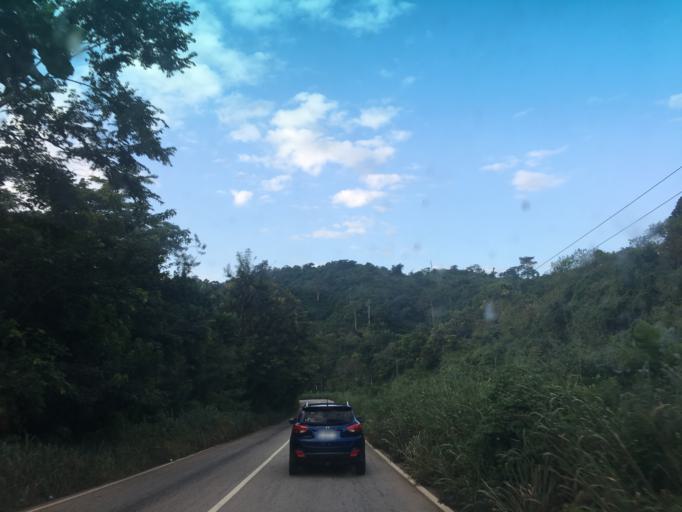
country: GH
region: Western
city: Bibiani
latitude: 6.4778
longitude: -2.3324
